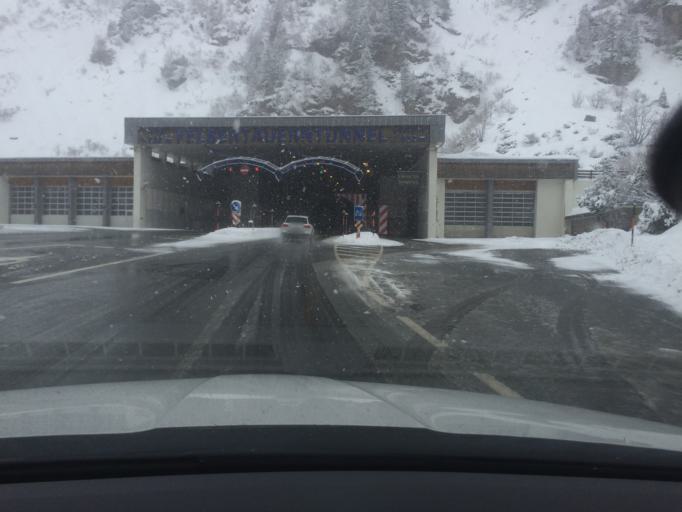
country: AT
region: Salzburg
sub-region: Politischer Bezirk Zell am See
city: Stuhlfelden
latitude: 47.1609
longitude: 12.5365
